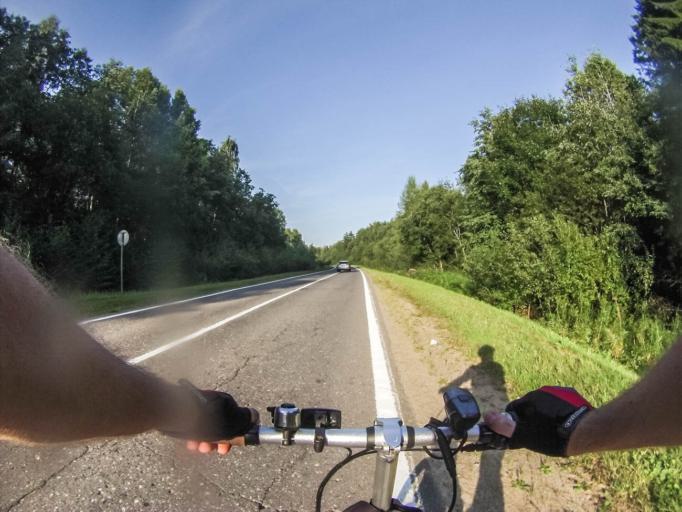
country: RU
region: Jaroslavl
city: Myshkin
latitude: 57.7162
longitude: 38.4049
